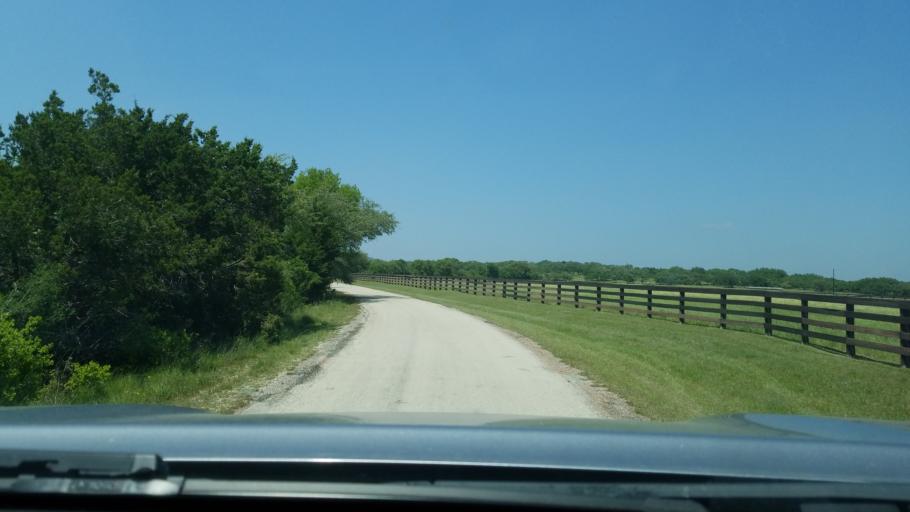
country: US
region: Texas
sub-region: Blanco County
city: Blanco
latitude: 30.0075
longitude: -98.4362
